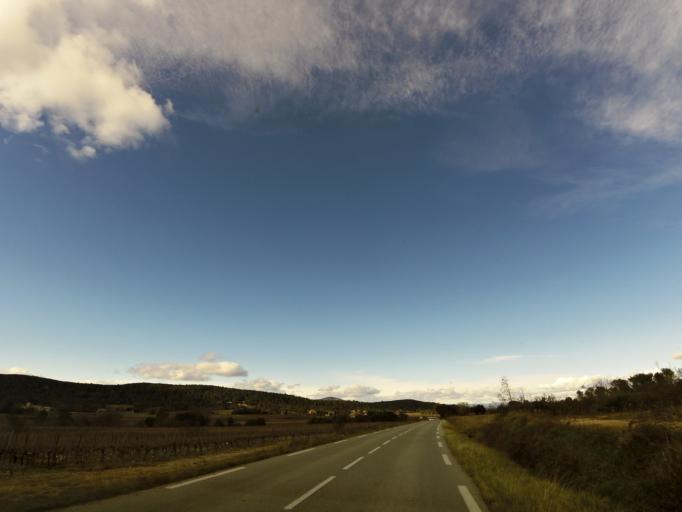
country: FR
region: Languedoc-Roussillon
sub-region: Departement du Gard
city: Quissac
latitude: 43.8483
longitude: 4.0194
